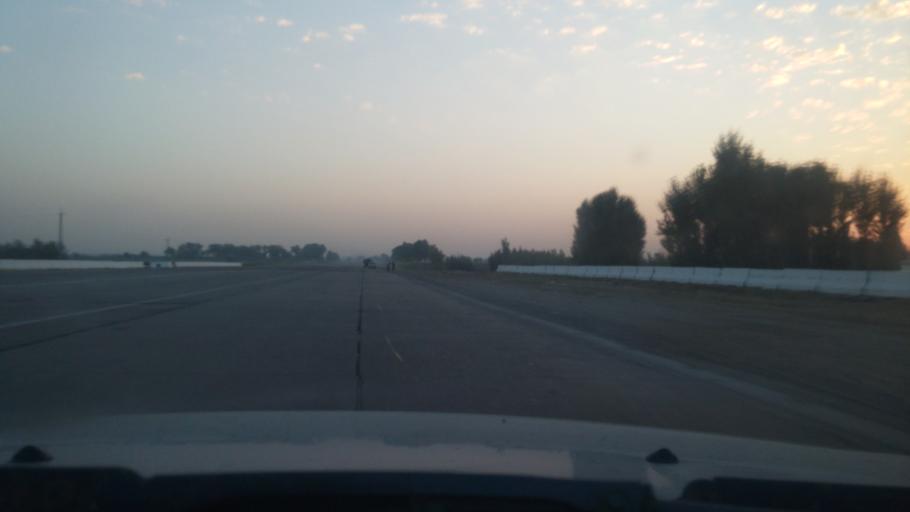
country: UZ
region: Toshkent
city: Chinoz
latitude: 40.9767
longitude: 68.7890
